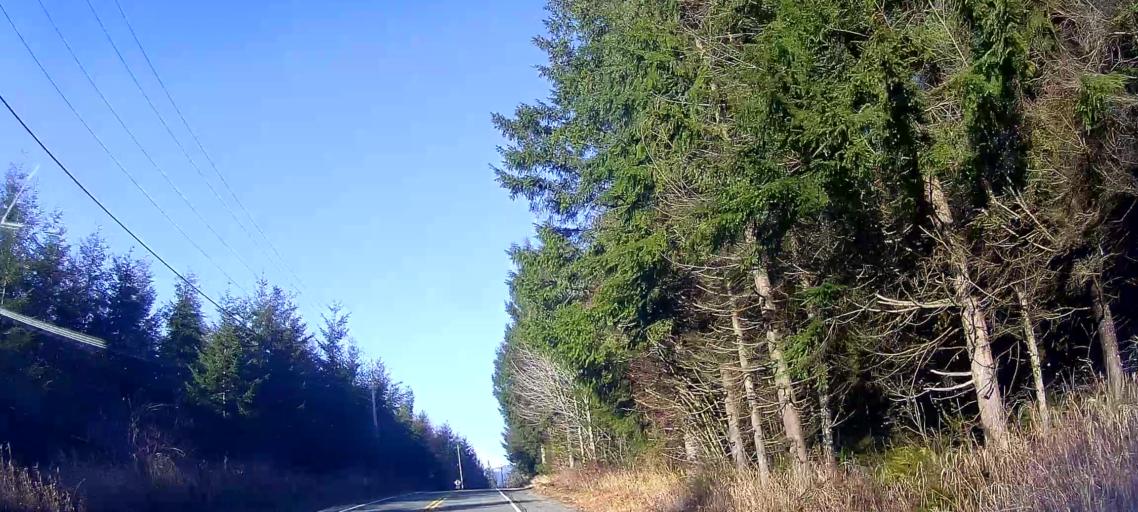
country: US
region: Washington
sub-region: Snohomish County
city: Darrington
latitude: 48.5543
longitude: -121.7656
